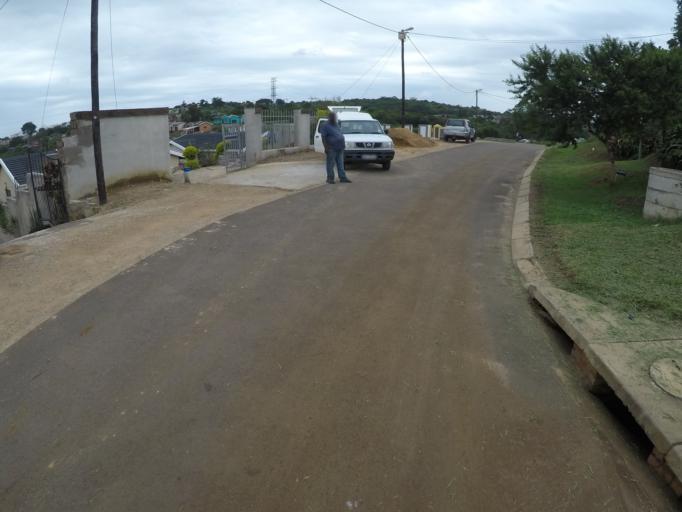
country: ZA
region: KwaZulu-Natal
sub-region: uThungulu District Municipality
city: Empangeni
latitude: -28.7713
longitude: 31.8729
